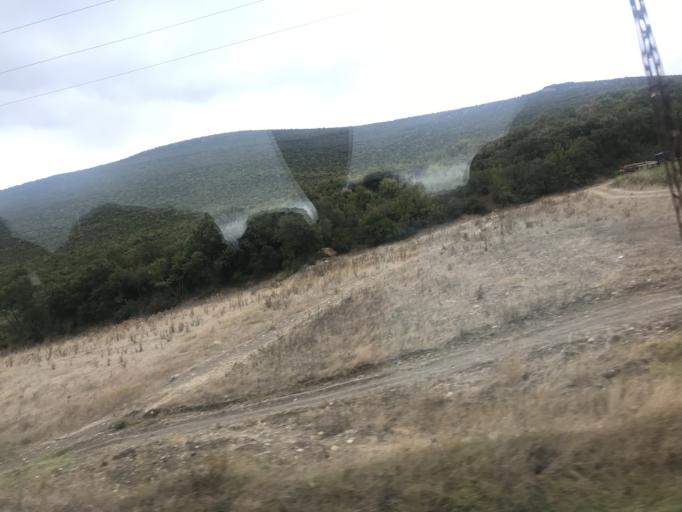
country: TR
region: Balikesir
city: Ergama
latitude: 39.6169
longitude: 27.5577
